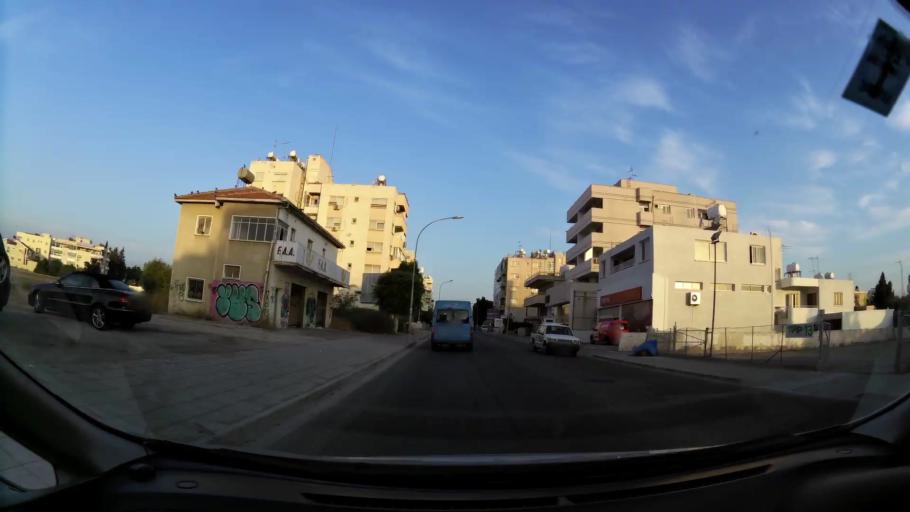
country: CY
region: Larnaka
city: Larnaca
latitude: 34.9213
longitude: 33.6147
